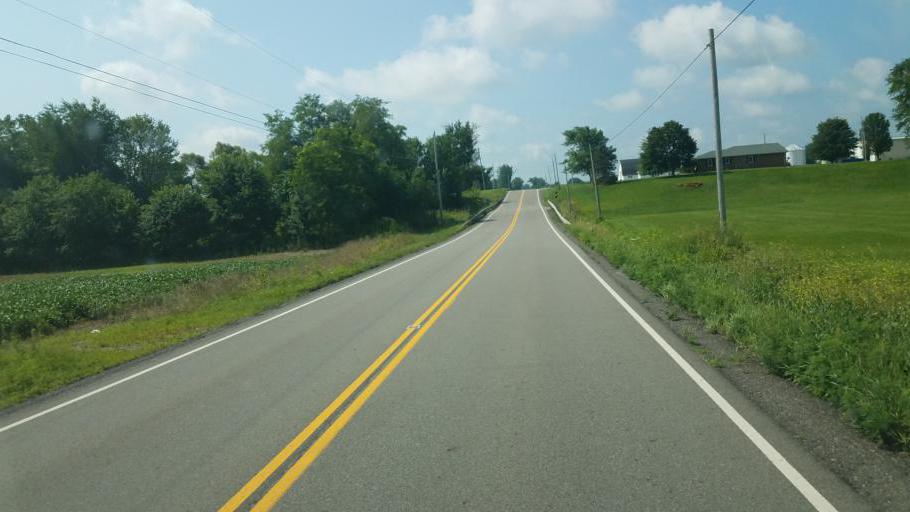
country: US
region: Ohio
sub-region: Licking County
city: Utica
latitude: 40.2741
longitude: -82.5158
